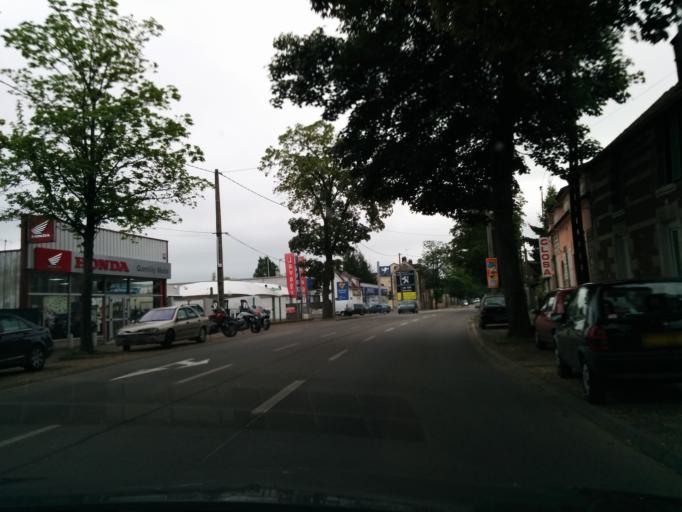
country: FR
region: Haute-Normandie
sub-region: Departement de l'Eure
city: Vernon
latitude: 49.0862
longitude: 1.4971
